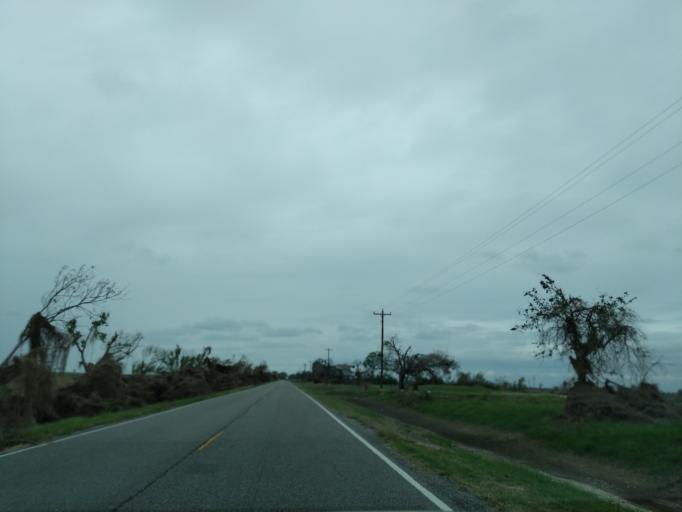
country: US
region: Louisiana
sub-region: Cameron Parish
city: Cameron
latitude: 29.7867
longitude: -93.1283
